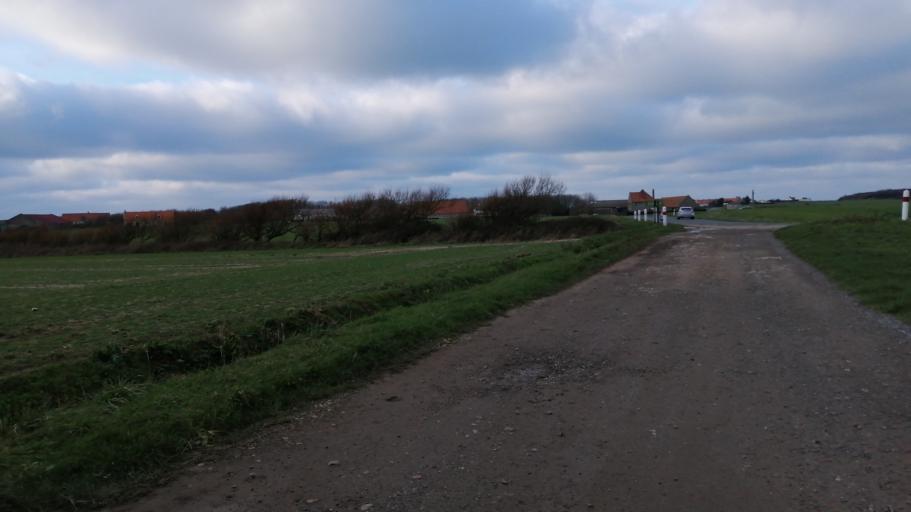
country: FR
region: Nord-Pas-de-Calais
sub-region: Departement du Pas-de-Calais
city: Ambleteuse
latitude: 50.8512
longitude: 1.5956
